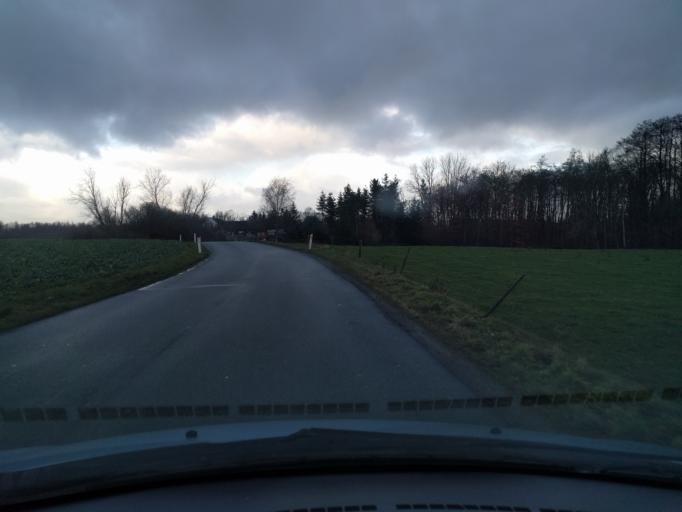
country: DK
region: South Denmark
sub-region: Kerteminde Kommune
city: Langeskov
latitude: 55.3662
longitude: 10.5873
